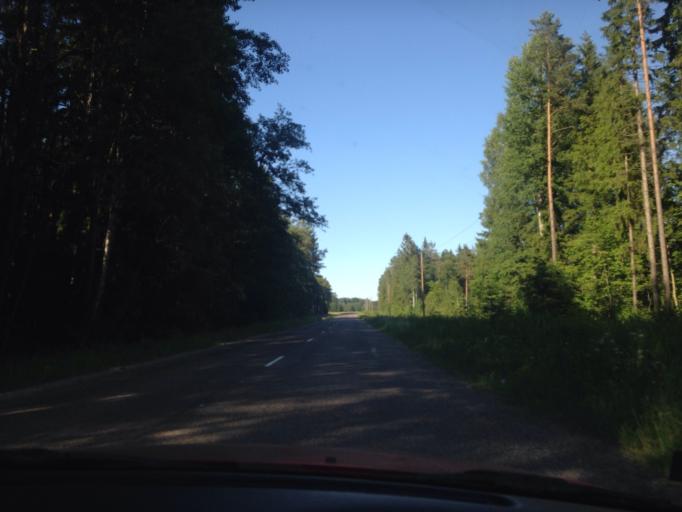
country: LV
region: Saulkrastu
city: Saulkrasti
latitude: 57.2465
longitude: 24.4934
